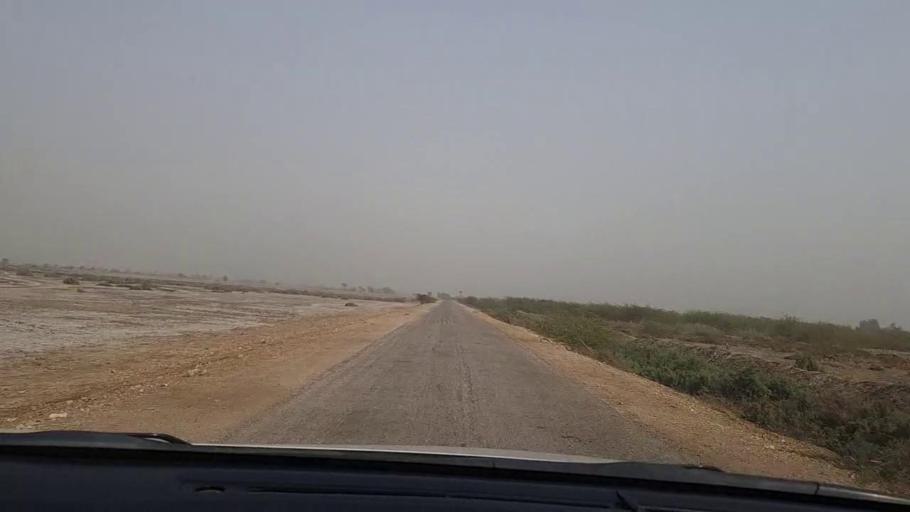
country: PK
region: Sindh
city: Samaro
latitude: 25.3836
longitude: 69.3584
